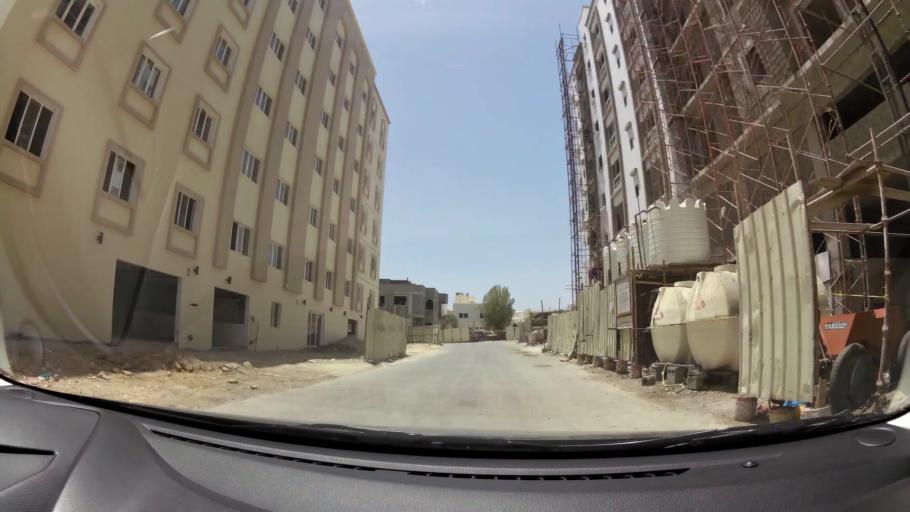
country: OM
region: Muhafazat Masqat
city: Muscat
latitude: 23.6223
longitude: 58.5018
